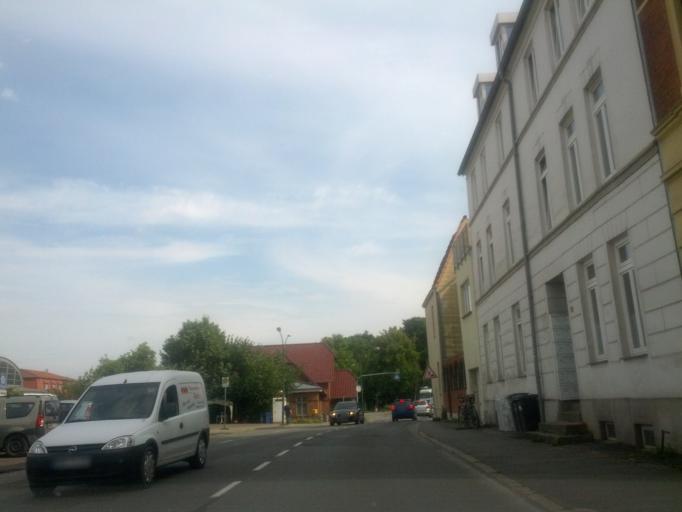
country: DE
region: Mecklenburg-Vorpommern
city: Wismar
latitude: 53.8966
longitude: 11.4679
